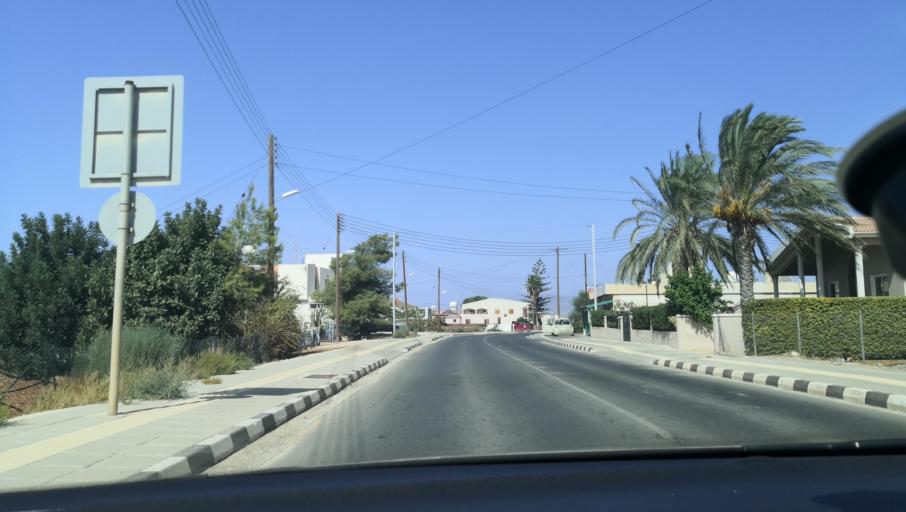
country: CY
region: Lefkosia
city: Kokkinotrimithia
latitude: 35.1196
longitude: 33.2093
